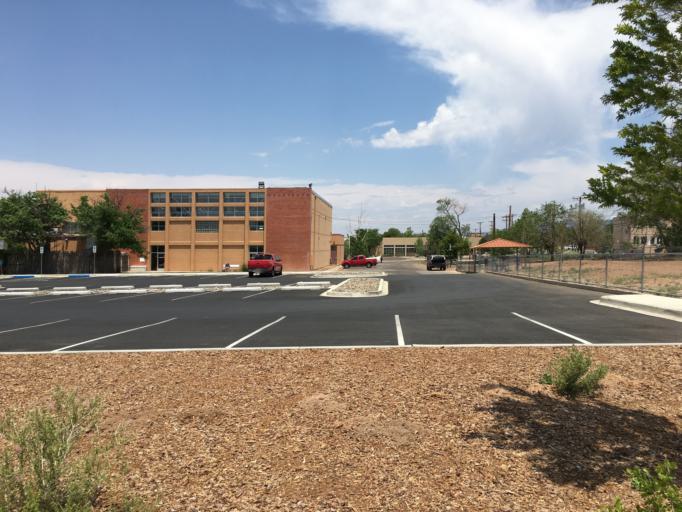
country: US
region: New Mexico
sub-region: Santa Fe County
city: Santa Fe
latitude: 35.6703
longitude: -105.9516
